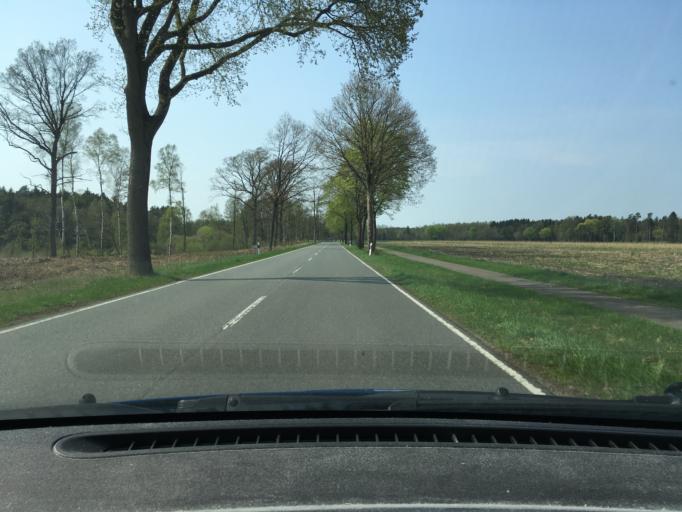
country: DE
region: Lower Saxony
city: Fassberg
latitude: 52.8850
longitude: 10.1821
